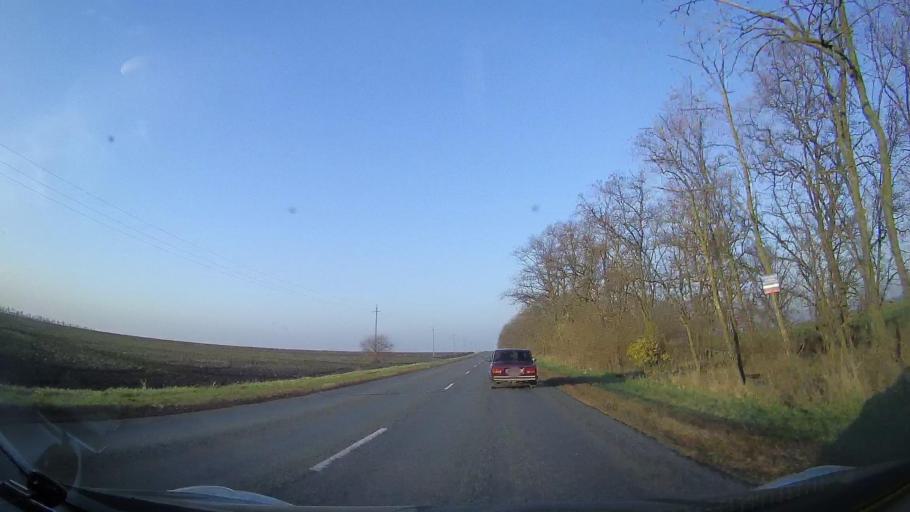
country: RU
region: Rostov
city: Ol'ginskaya
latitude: 47.0848
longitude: 39.9777
